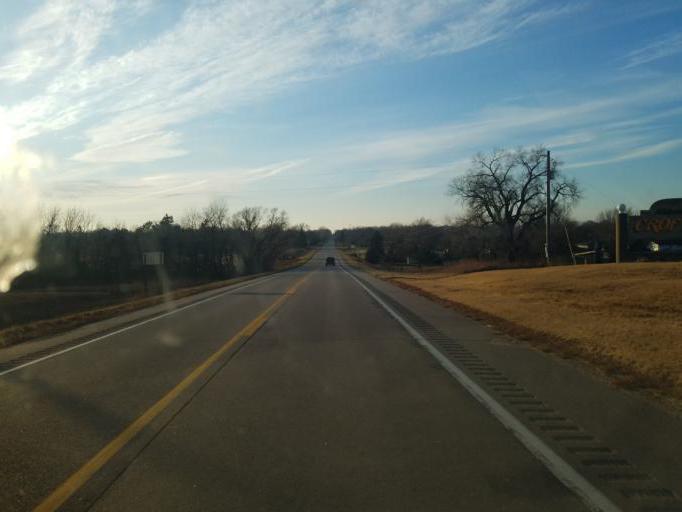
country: US
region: South Dakota
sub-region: Yankton County
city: Yankton
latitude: 42.7289
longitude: -97.4866
